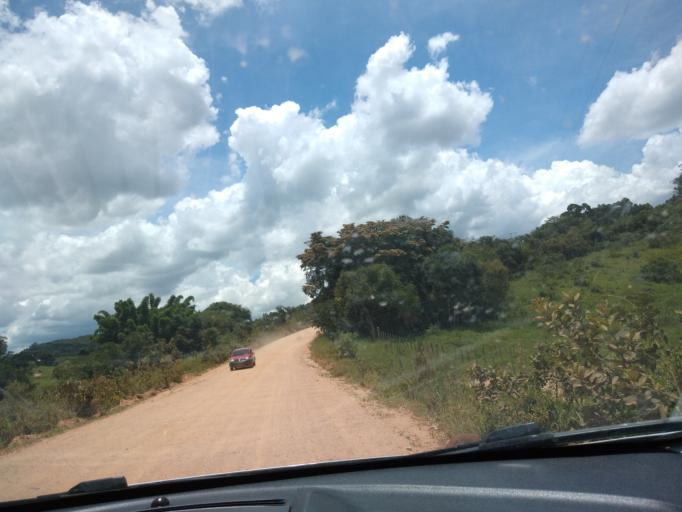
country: BR
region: Minas Gerais
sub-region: Sao Joao Del Rei
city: Sao Joao del Rei
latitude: -20.8911
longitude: -44.3077
